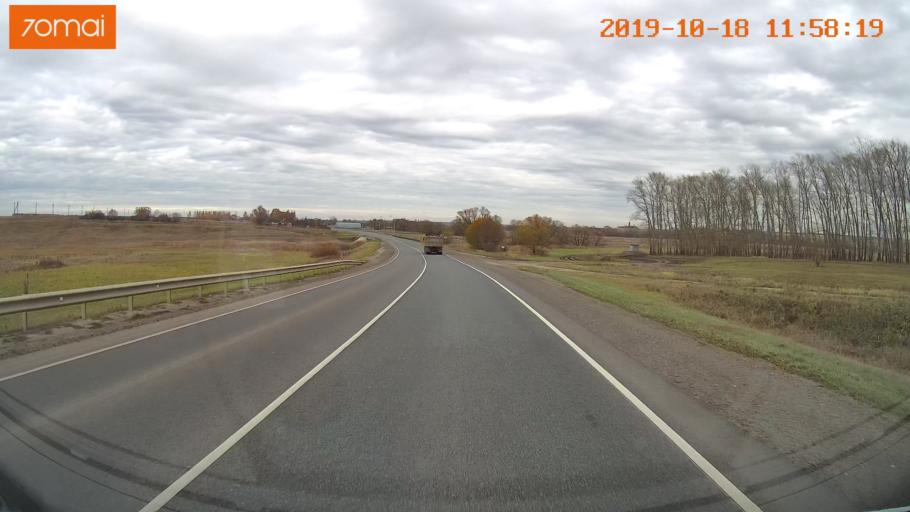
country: RU
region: Rjazan
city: Mikhaylov
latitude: 54.2703
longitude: 39.1658
